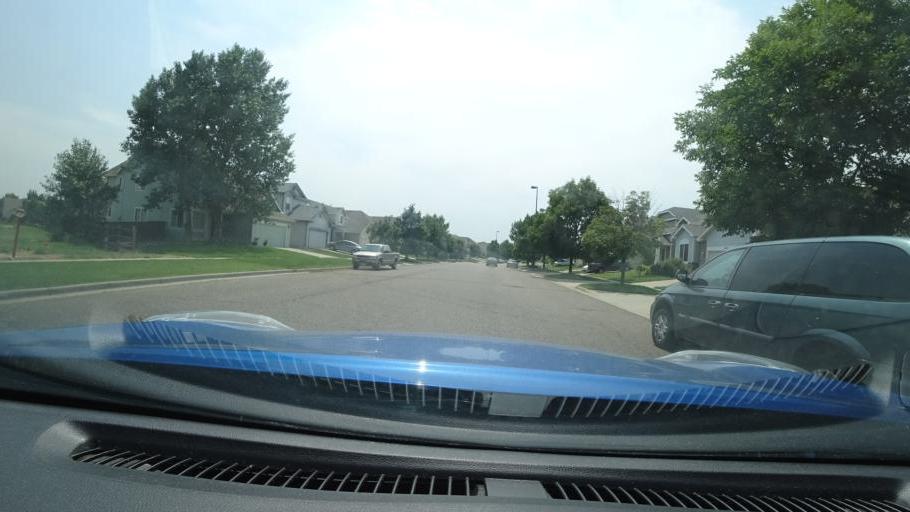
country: US
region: Colorado
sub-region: Adams County
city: Aurora
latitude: 39.7739
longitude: -104.7429
